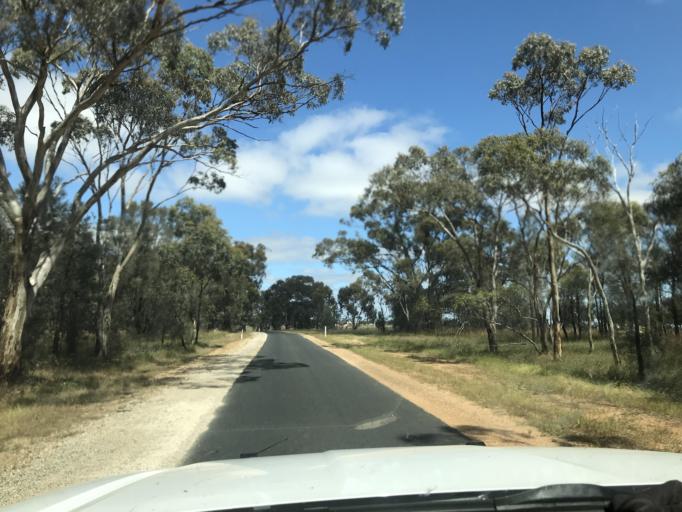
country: AU
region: South Australia
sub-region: Tatiara
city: Bordertown
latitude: -36.3064
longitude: 141.0631
